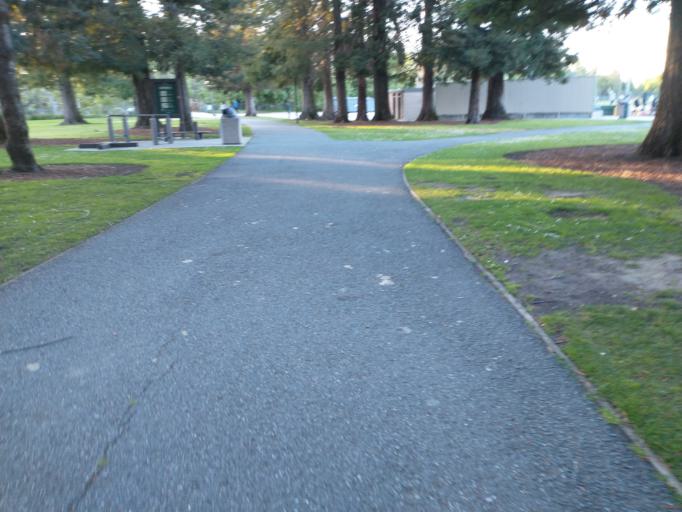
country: US
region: California
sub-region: Santa Clara County
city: Santa Clara
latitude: 37.3424
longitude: -121.9749
